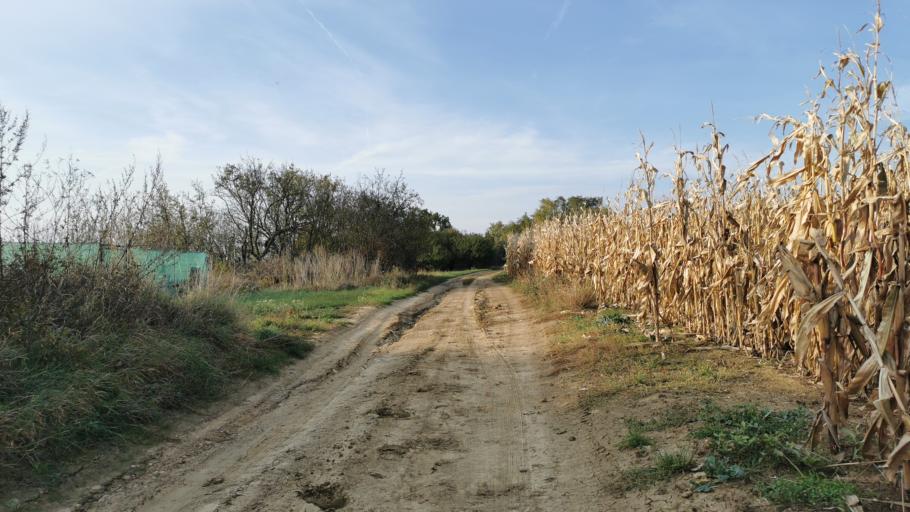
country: SK
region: Trnavsky
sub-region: Okres Skalica
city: Skalica
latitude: 48.8193
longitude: 17.2430
